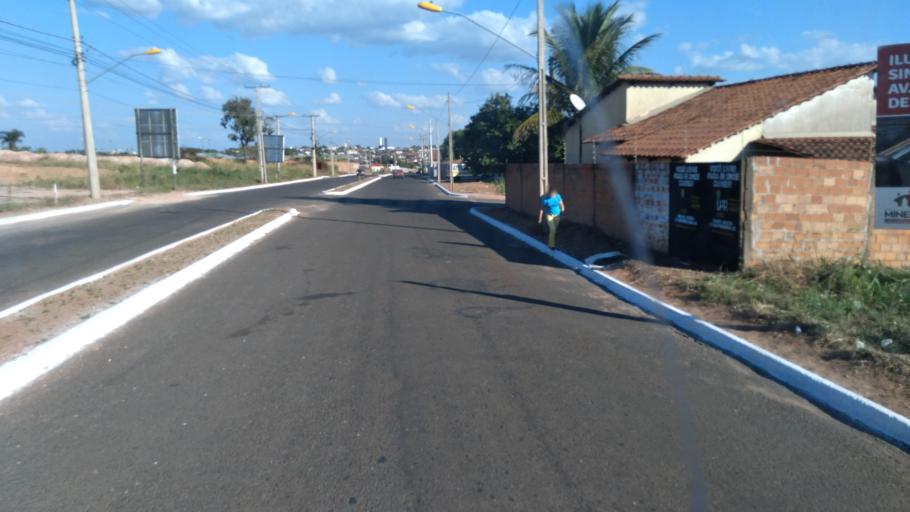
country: BR
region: Goias
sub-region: Mineiros
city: Mineiros
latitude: -17.5574
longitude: -52.5407
